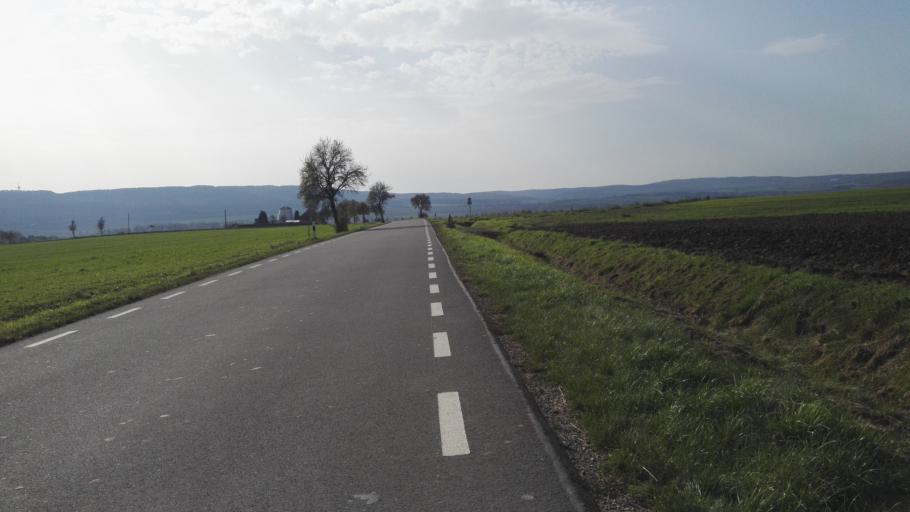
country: DE
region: Lower Saxony
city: Bad Salzdetfurth
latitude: 52.1154
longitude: 10.0193
